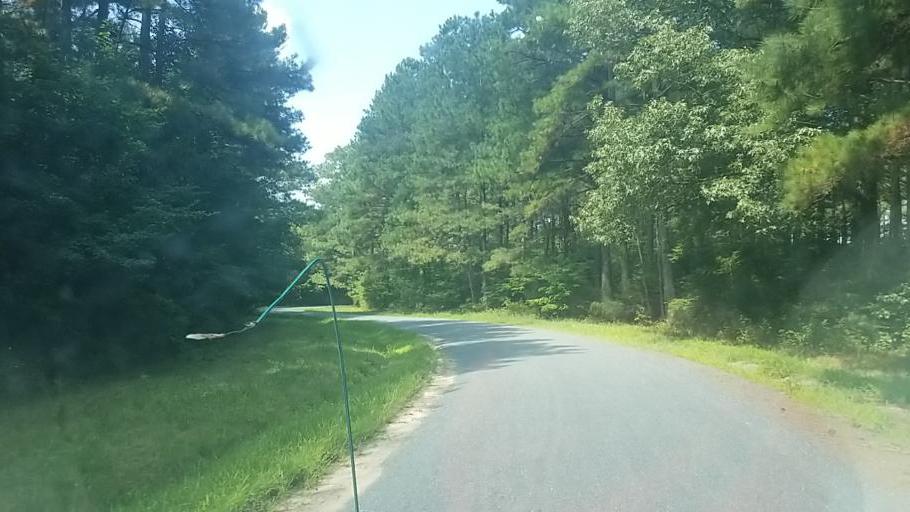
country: US
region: Maryland
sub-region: Worcester County
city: Berlin
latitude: 38.2875
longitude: -75.3100
